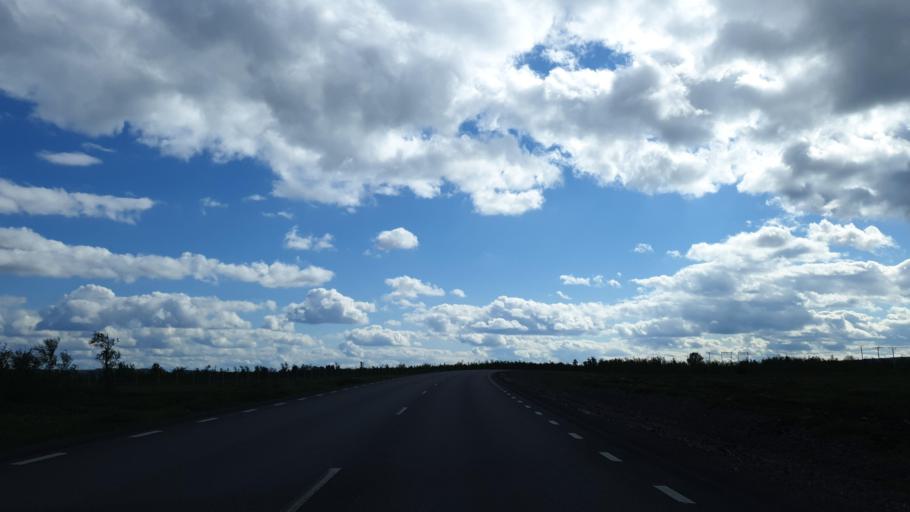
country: SE
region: Norrbotten
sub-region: Kiruna Kommun
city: Kiruna
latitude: 67.8314
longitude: 20.3039
